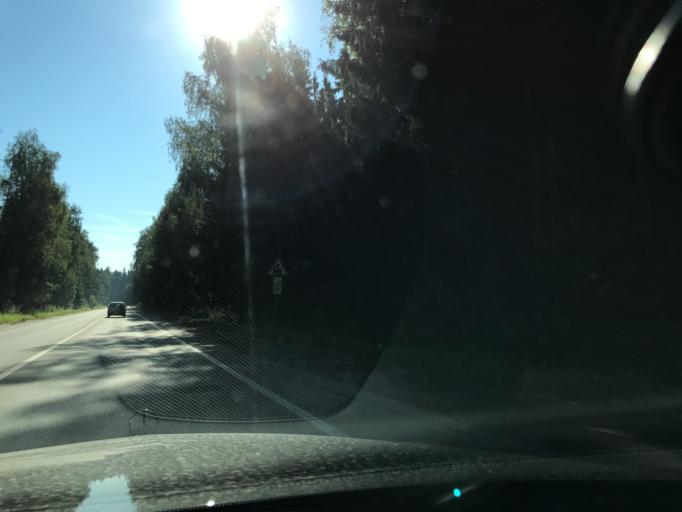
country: RU
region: Moskovskaya
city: Chernogolovka
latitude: 55.9846
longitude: 38.3430
